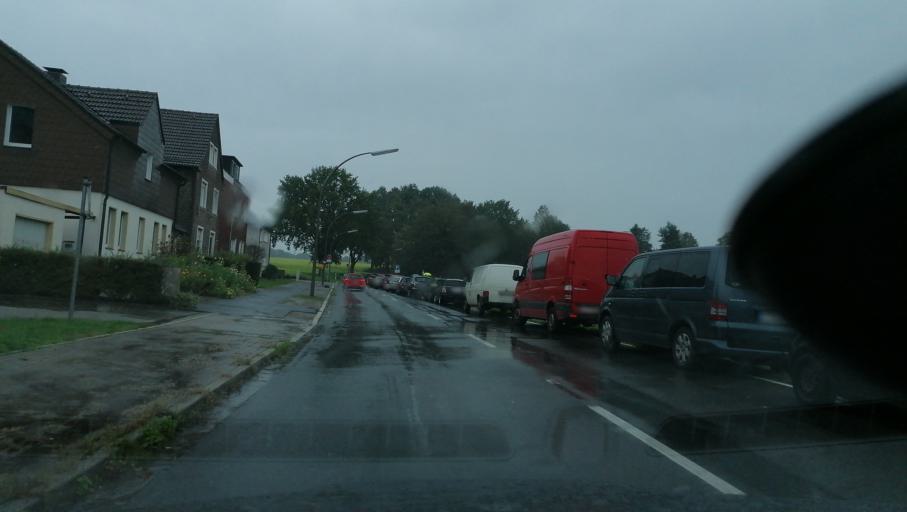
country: DE
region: North Rhine-Westphalia
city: Herten
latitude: 51.6109
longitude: 7.1674
